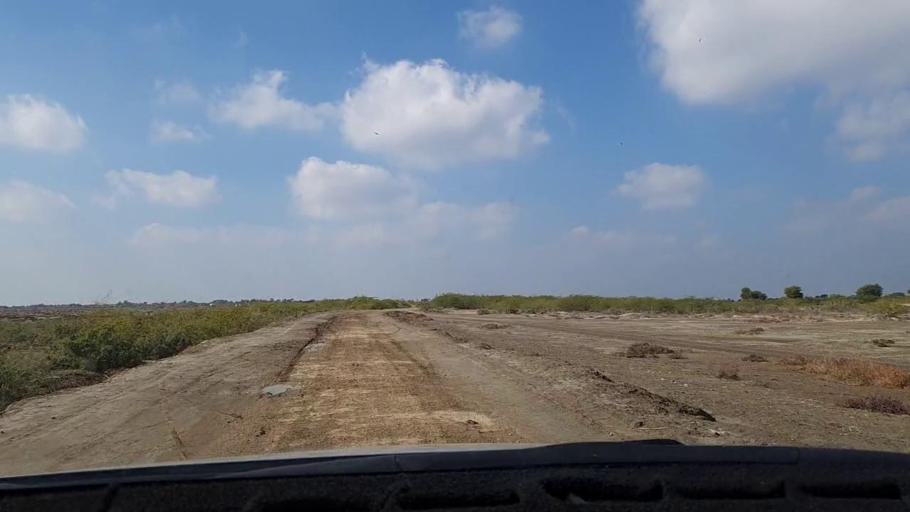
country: PK
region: Sindh
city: Tando Mittha Khan
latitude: 25.7691
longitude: 69.2644
